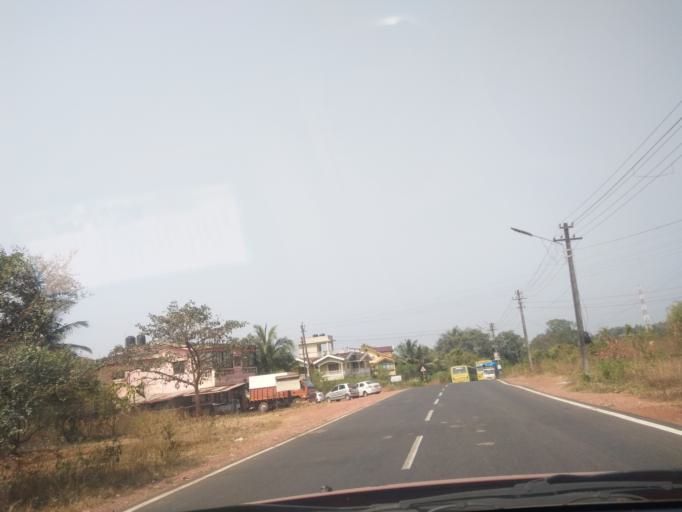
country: IN
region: Goa
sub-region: North Goa
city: Aldona
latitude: 15.6248
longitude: 73.8797
